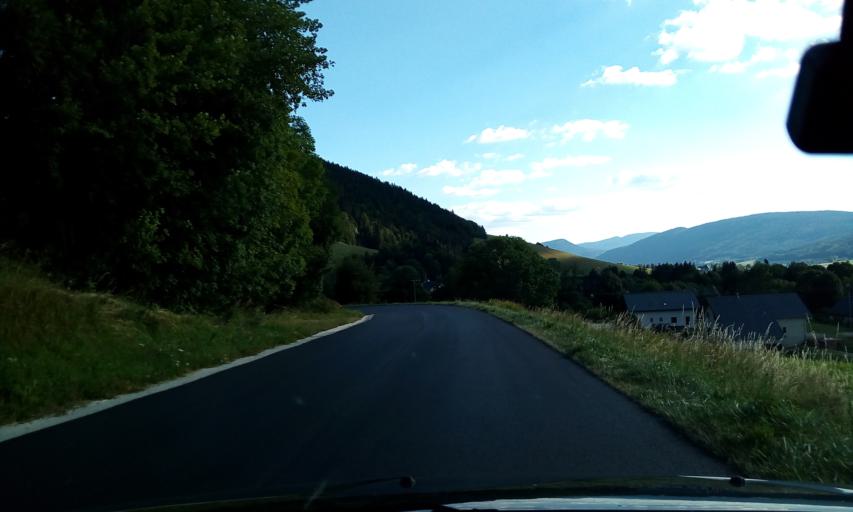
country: FR
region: Rhone-Alpes
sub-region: Departement de l'Isere
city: Lans-en-Vercors
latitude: 45.1298
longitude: 5.5994
